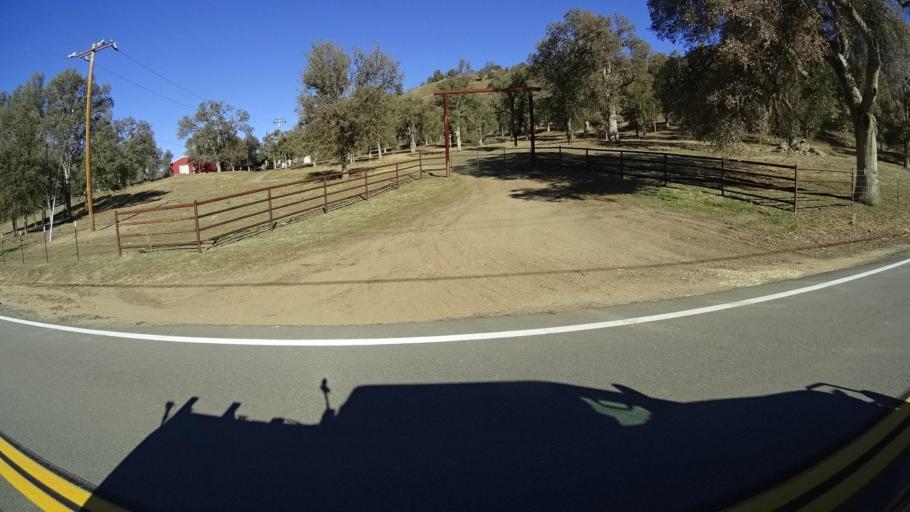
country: US
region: California
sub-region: Kern County
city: Alta Sierra
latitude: 35.7116
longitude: -118.7340
